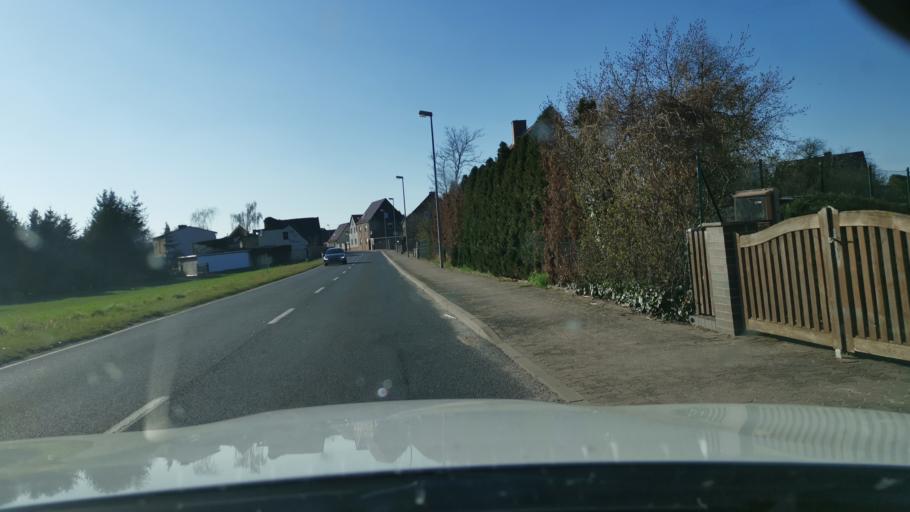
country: DE
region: Saxony-Anhalt
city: Muldenstein
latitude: 51.6793
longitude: 12.3305
